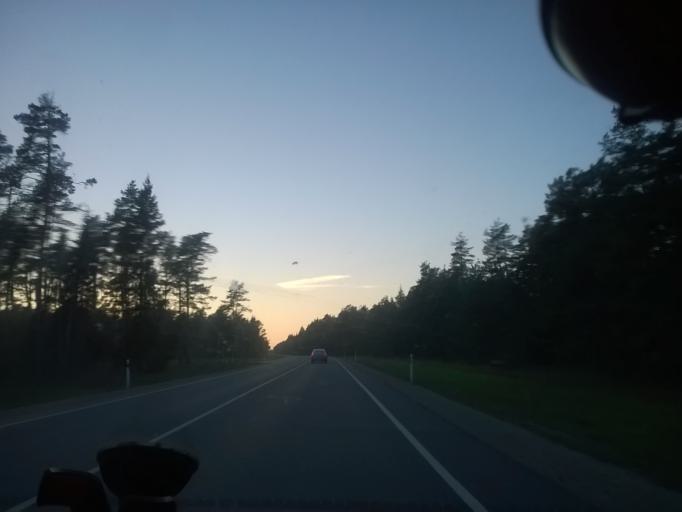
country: EE
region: Laeaene
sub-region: Lihula vald
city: Lihula
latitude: 58.9739
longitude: 23.9291
